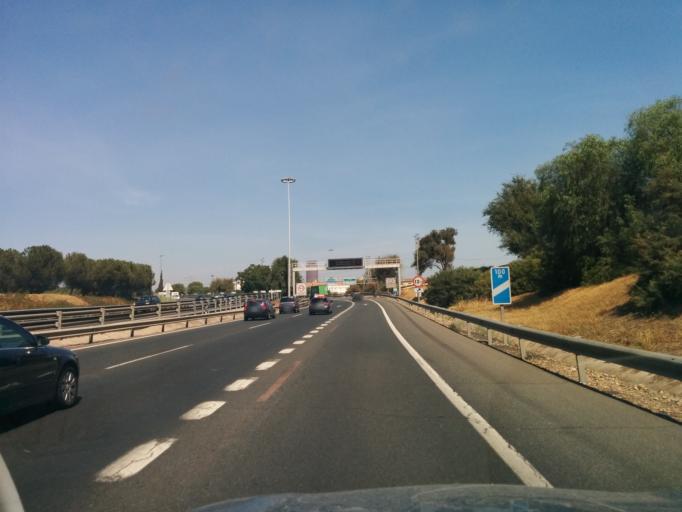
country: ES
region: Andalusia
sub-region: Provincia de Sevilla
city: San Juan de Aznalfarache
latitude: 37.3694
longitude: -6.0141
